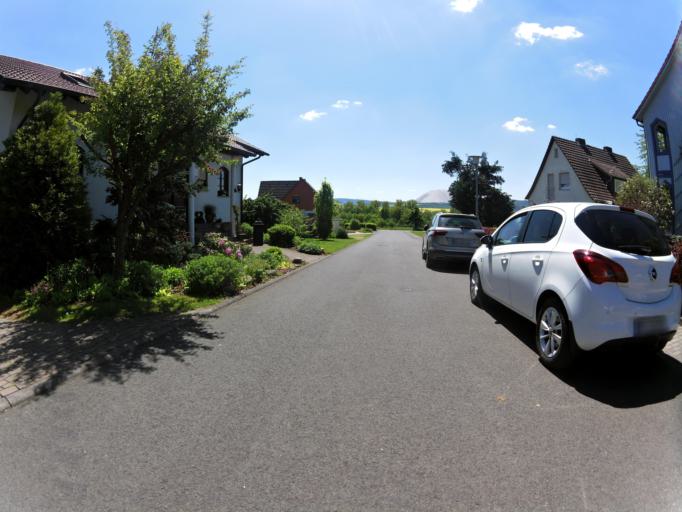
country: DE
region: Thuringia
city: Dankmarshausen
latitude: 50.9521
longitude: 10.0009
